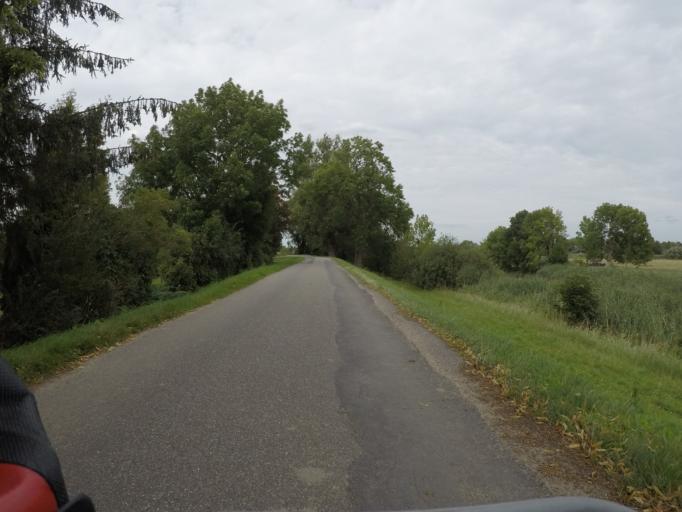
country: DE
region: Lower Saxony
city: Winsen
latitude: 53.3908
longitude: 10.2001
